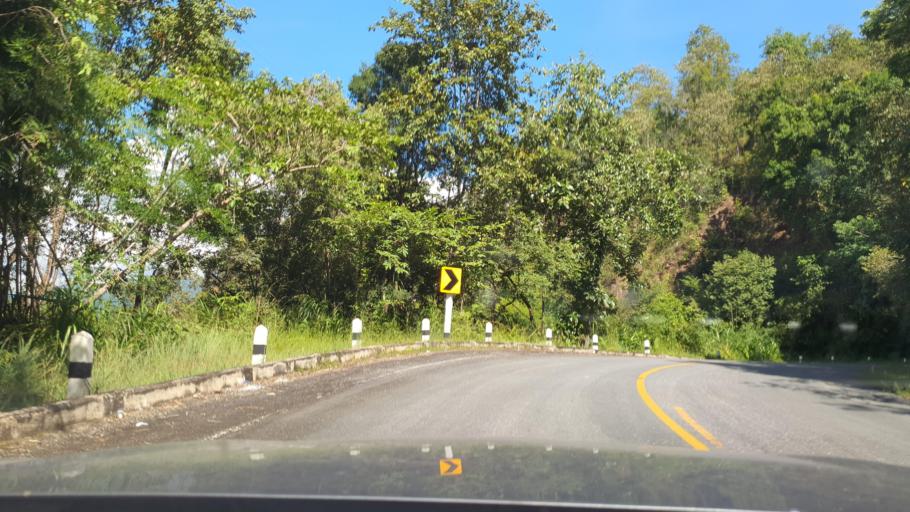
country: TH
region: Chiang Mai
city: Phrao
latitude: 19.3590
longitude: 99.2692
